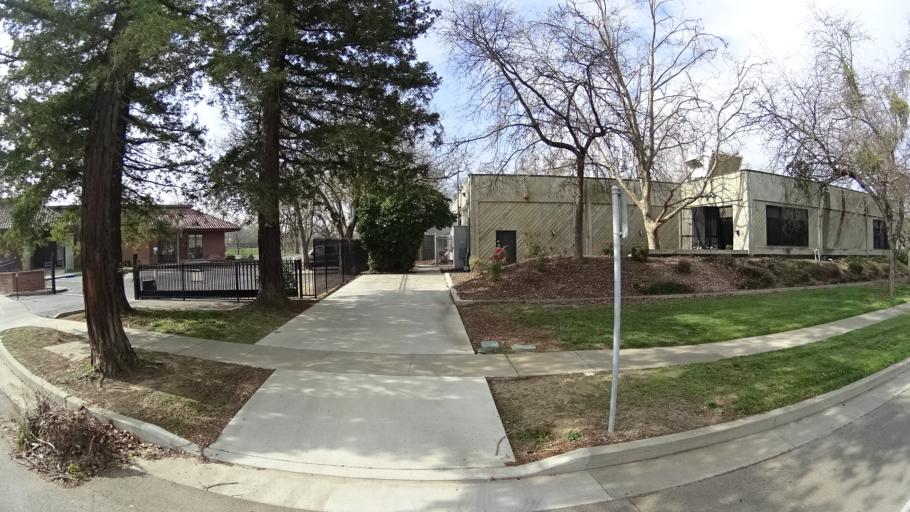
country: US
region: California
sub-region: Yolo County
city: Davis
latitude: 38.5374
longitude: -121.7324
